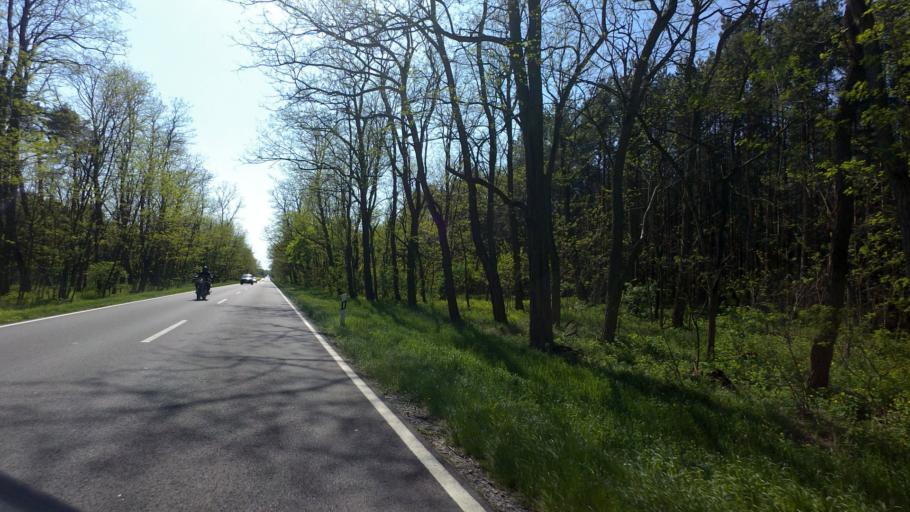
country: DE
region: Brandenburg
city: Neu Zauche
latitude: 52.0424
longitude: 14.1116
